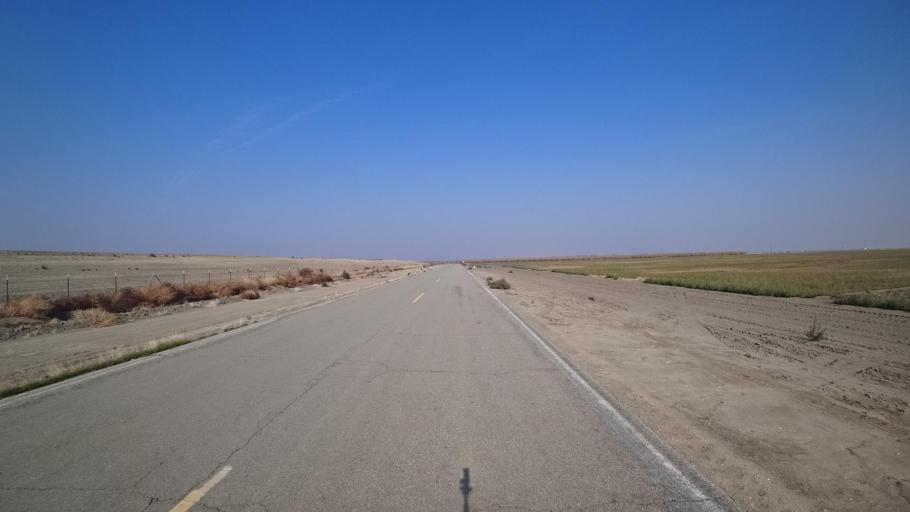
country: US
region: California
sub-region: Kern County
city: Buttonwillow
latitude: 35.3356
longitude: -119.3767
